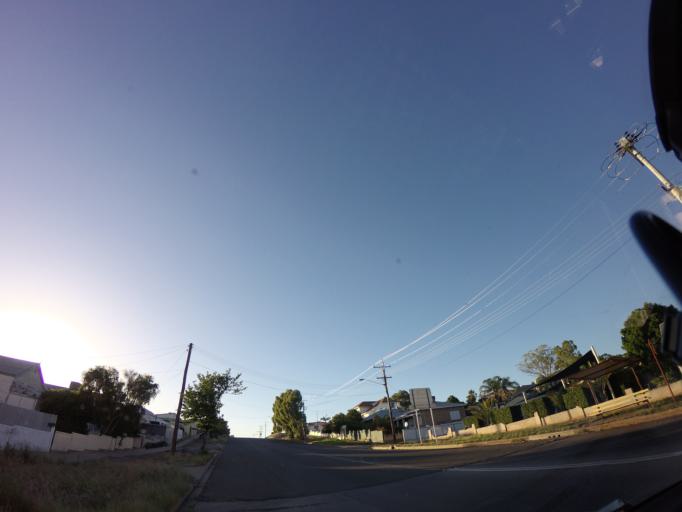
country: AU
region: New South Wales
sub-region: Broken Hill Municipality
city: Broken Hill
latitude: -31.9517
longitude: 141.4545
